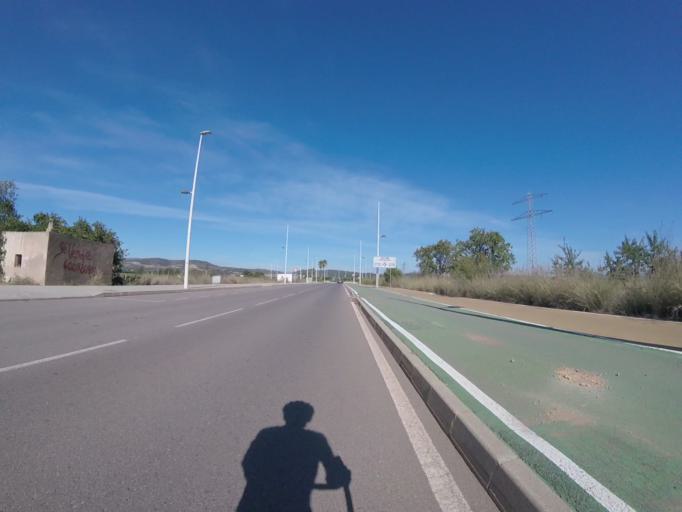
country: ES
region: Valencia
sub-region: Provincia de Castello
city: Torreblanca
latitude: 40.2168
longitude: 0.2202
